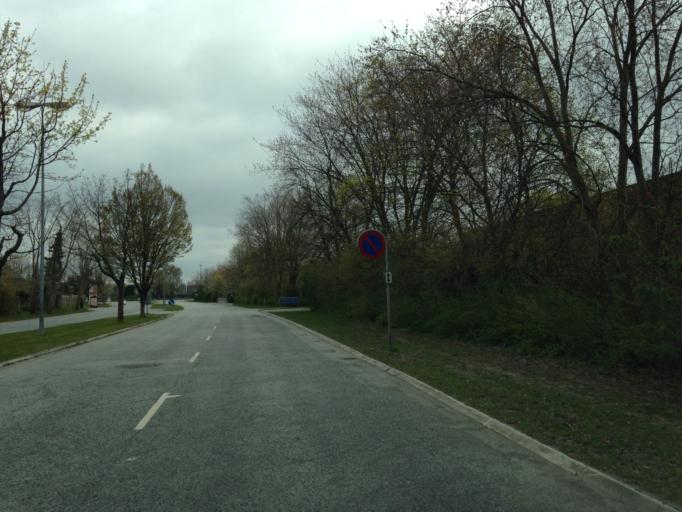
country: DK
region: Capital Region
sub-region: Ishoj Kommune
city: Ishoj
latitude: 55.6161
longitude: 12.3441
